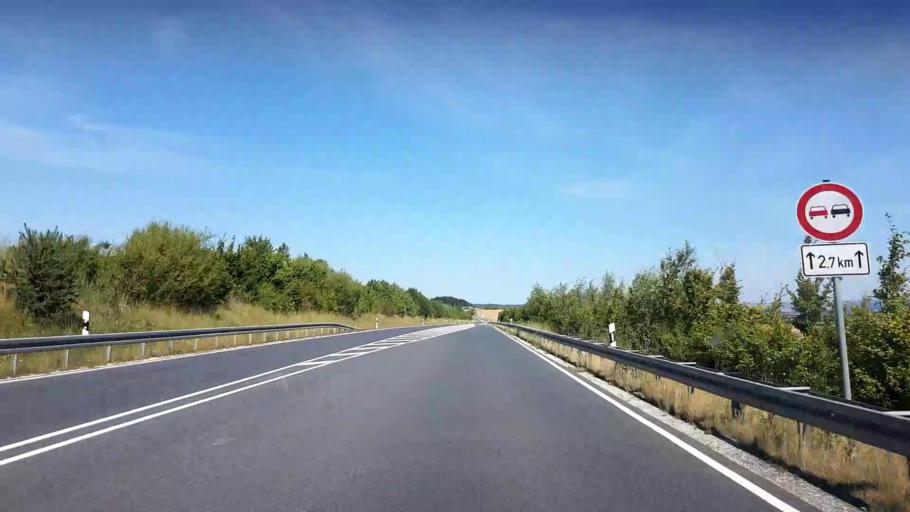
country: DE
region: Bavaria
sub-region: Upper Franconia
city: Untersiemau
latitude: 50.1713
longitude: 10.9906
